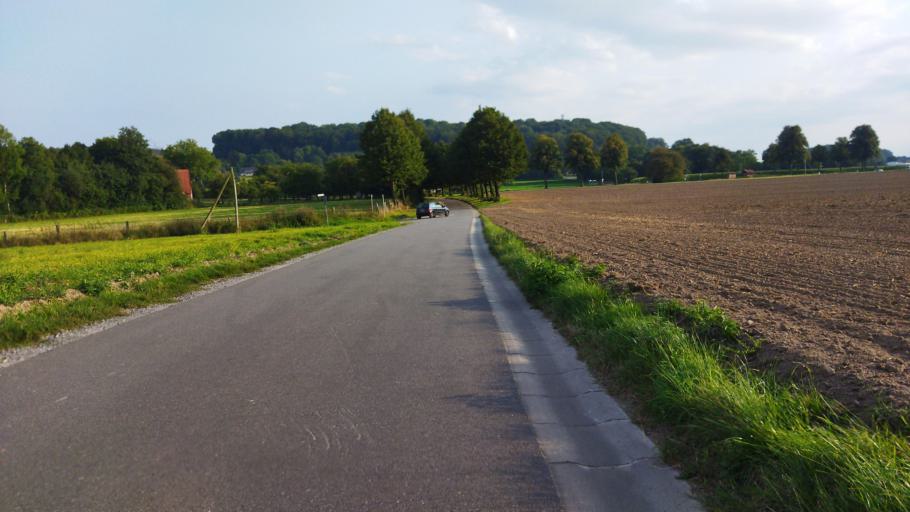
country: DE
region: Lower Saxony
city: Hagen
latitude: 52.2055
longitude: 7.9983
